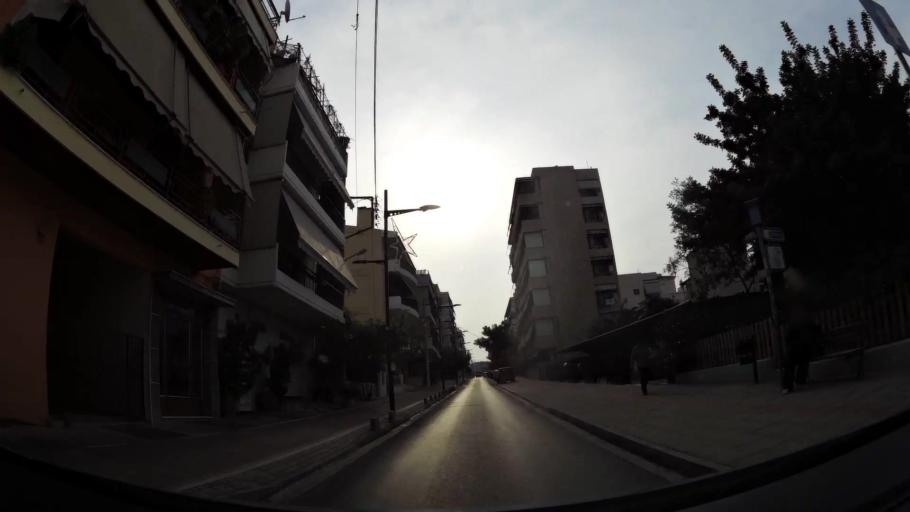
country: GR
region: Attica
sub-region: Nomarchia Athinas
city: Agios Dimitrios
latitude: 37.9323
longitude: 23.7247
